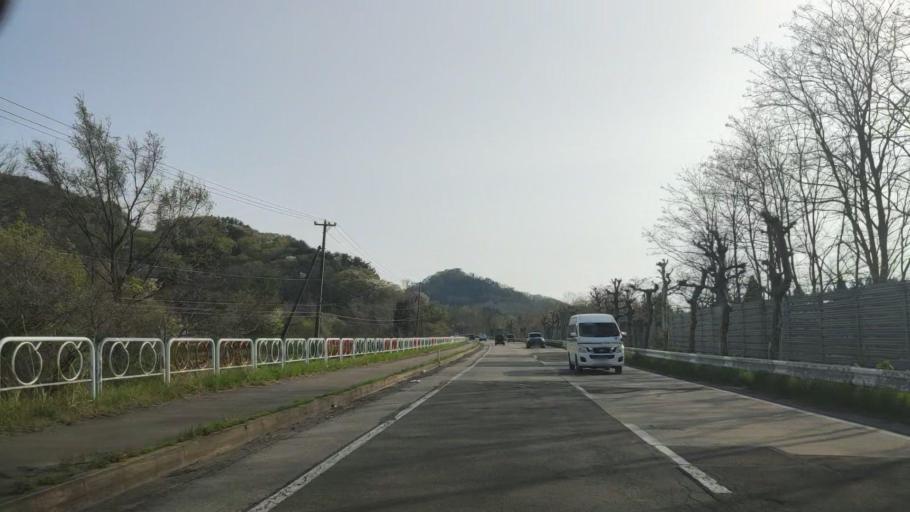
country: JP
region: Aomori
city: Aomori Shi
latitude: 40.8690
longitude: 140.8485
